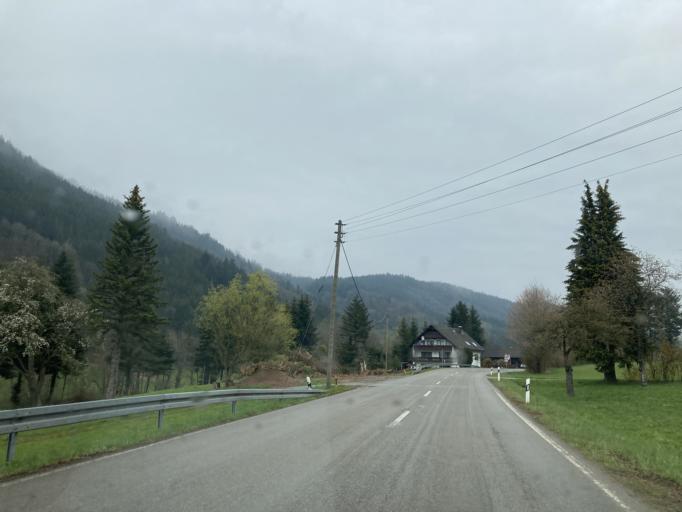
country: DE
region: Baden-Wuerttemberg
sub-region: Freiburg Region
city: Muhlenbach
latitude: 48.2067
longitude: 8.1259
